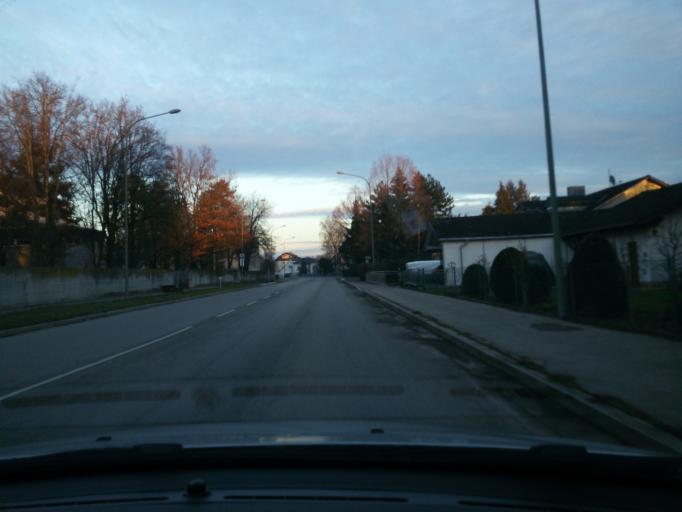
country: DE
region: Bavaria
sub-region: Swabia
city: Schwabmunchen
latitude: 48.1752
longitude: 10.7458
